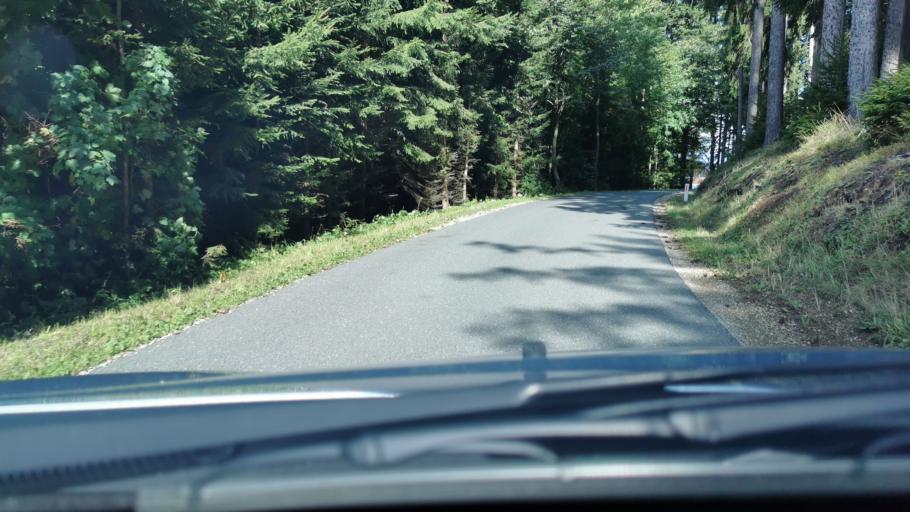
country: AT
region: Styria
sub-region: Politischer Bezirk Weiz
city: Koglhof
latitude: 47.3166
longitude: 15.7066
